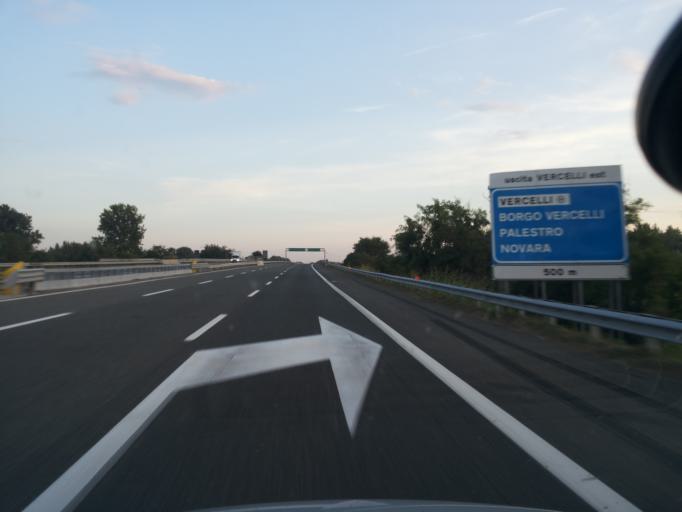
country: IT
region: Piedmont
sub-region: Provincia di Vercelli
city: Borgo Vercelli
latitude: 45.3726
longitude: 8.4859
